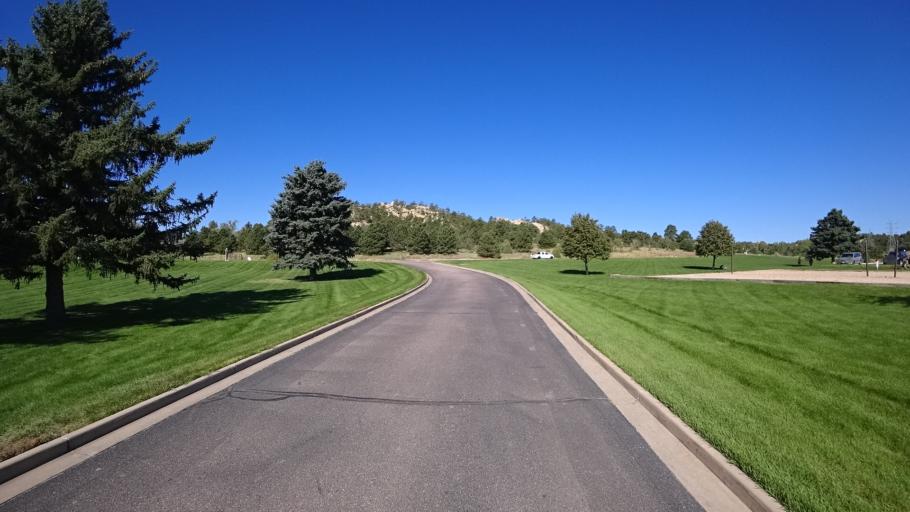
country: US
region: Colorado
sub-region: El Paso County
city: Cimarron Hills
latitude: 38.8685
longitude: -104.7611
